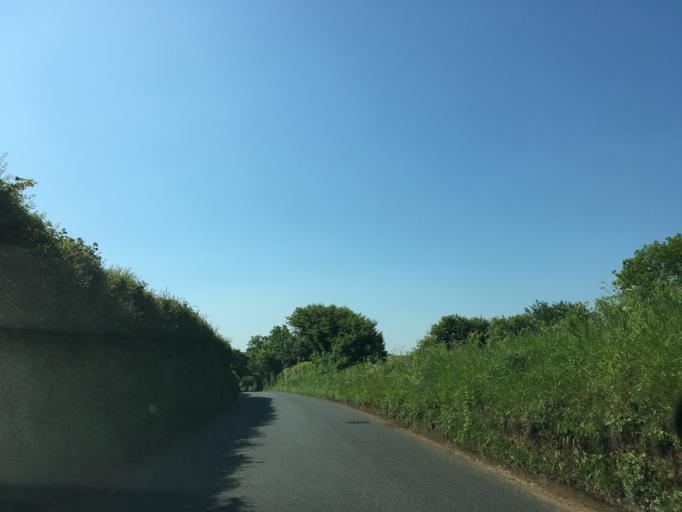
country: GB
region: England
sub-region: Isle of Wight
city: Newchurch
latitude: 50.6741
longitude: -1.2110
